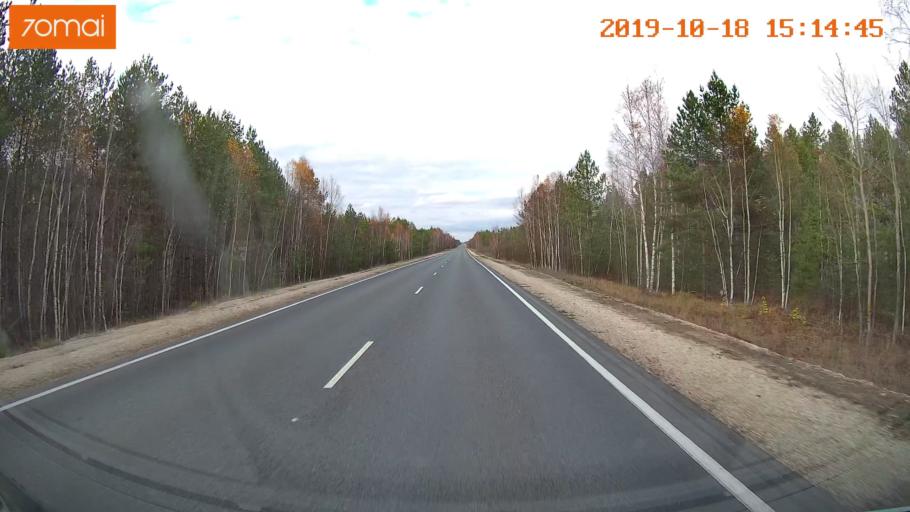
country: RU
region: Vladimir
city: Gus'-Khrustal'nyy
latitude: 55.6077
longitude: 40.7209
